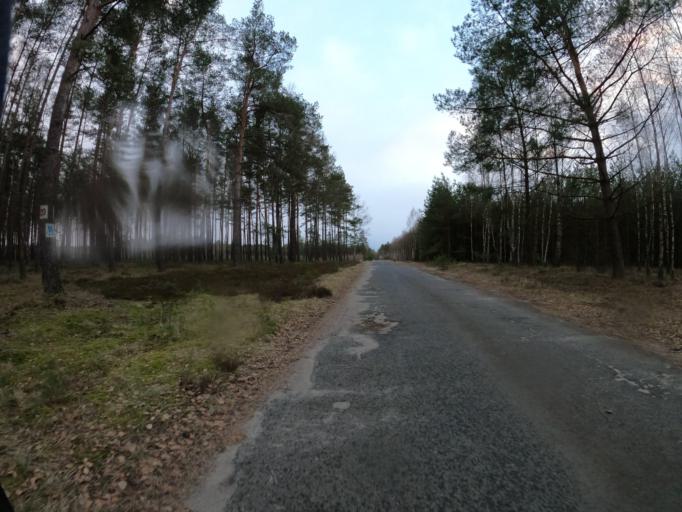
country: PL
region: West Pomeranian Voivodeship
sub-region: Powiat szczecinecki
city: Borne Sulinowo
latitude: 53.5499
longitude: 16.5813
